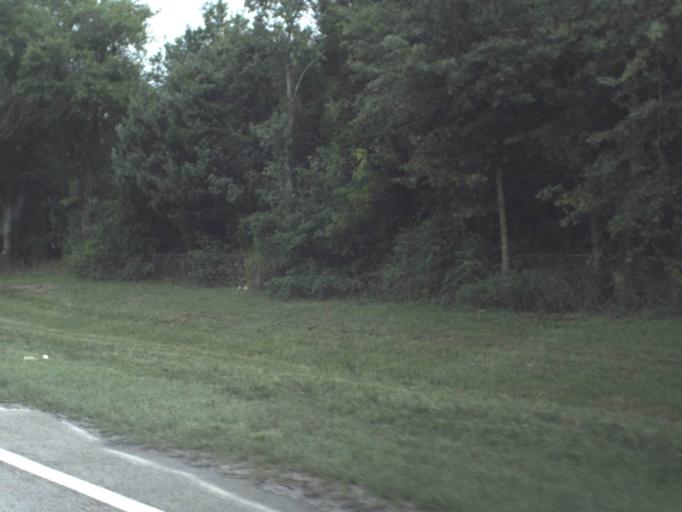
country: US
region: Florida
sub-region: Alachua County
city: Waldo
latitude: 29.8637
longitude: -82.1535
